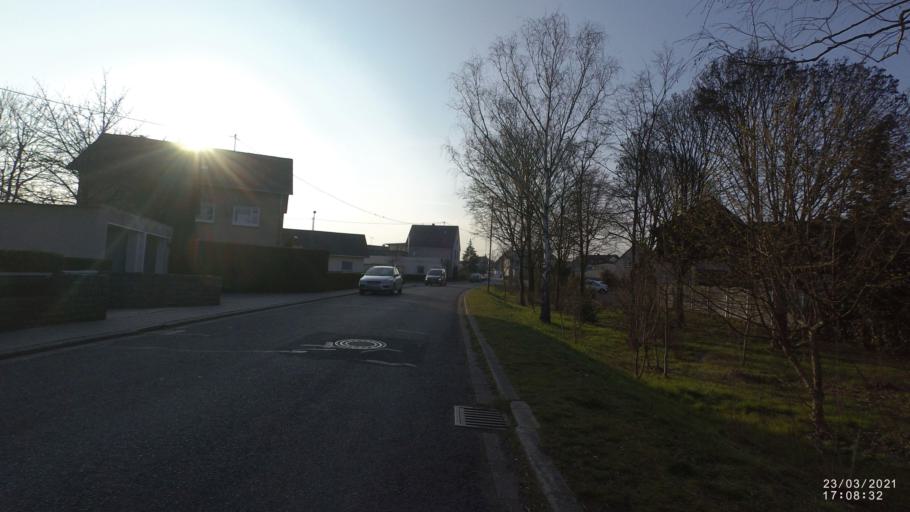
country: DE
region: Rheinland-Pfalz
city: Plaidt
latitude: 50.3911
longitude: 7.3995
